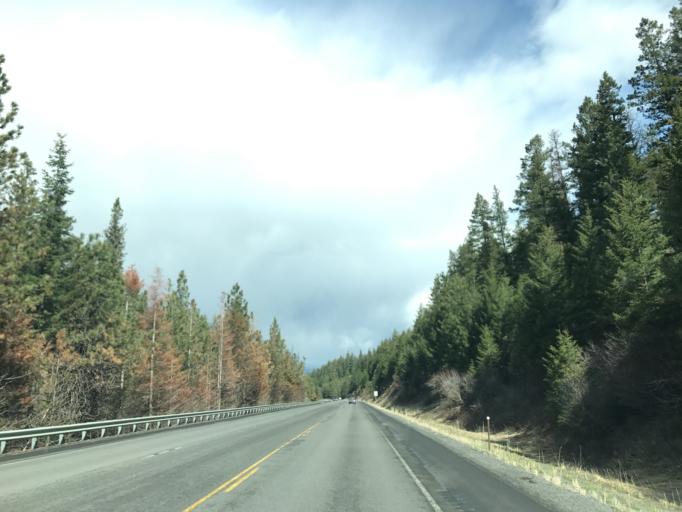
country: US
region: Idaho
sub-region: Idaho County
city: Grangeville
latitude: 45.8521
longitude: -116.2383
